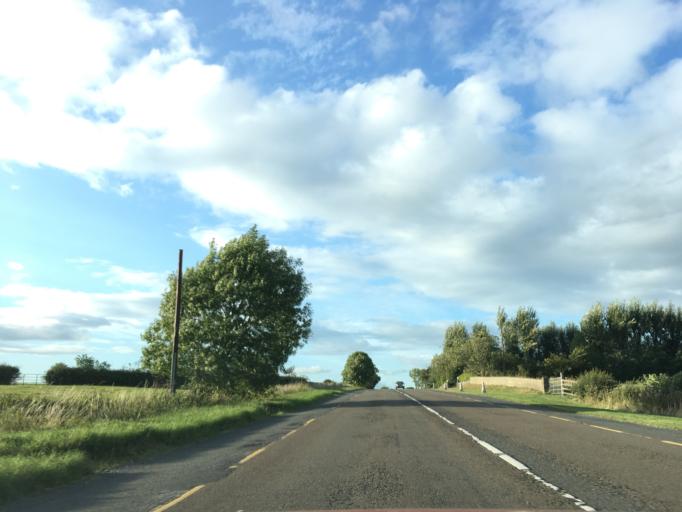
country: IE
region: Munster
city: Cashel
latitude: 52.4895
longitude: -7.8906
